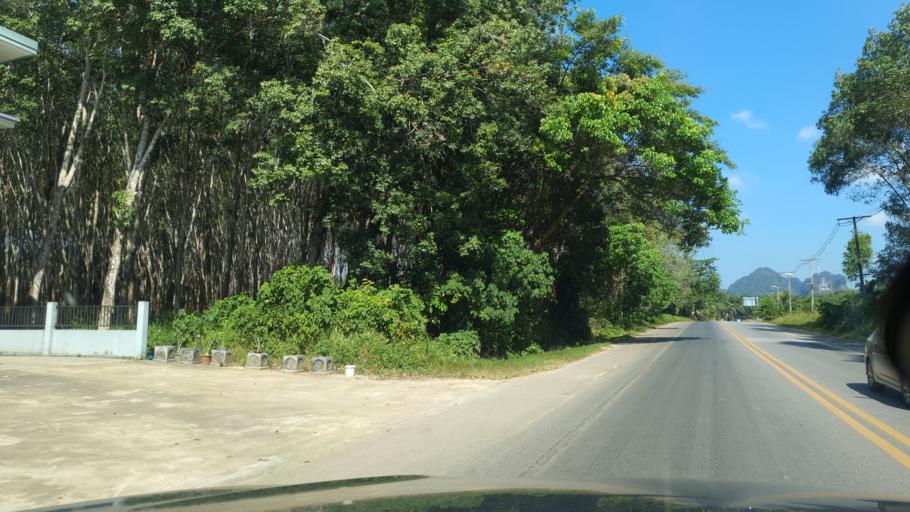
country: TH
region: Krabi
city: Krabi
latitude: 8.0652
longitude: 98.8593
